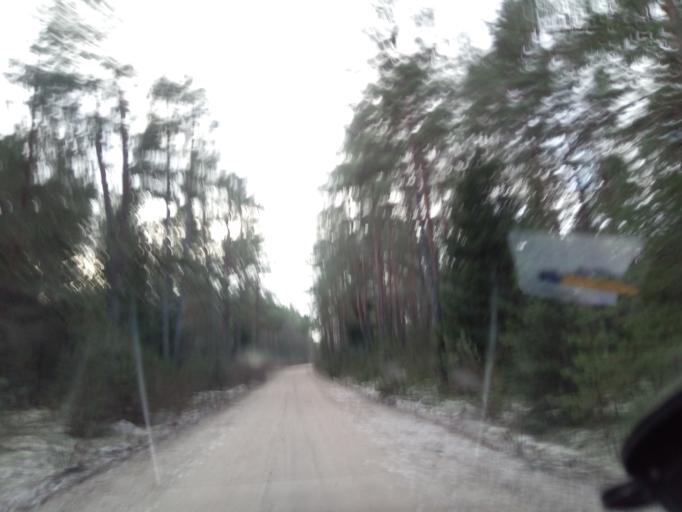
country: LT
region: Alytaus apskritis
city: Varena
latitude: 53.9702
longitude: 24.3209
